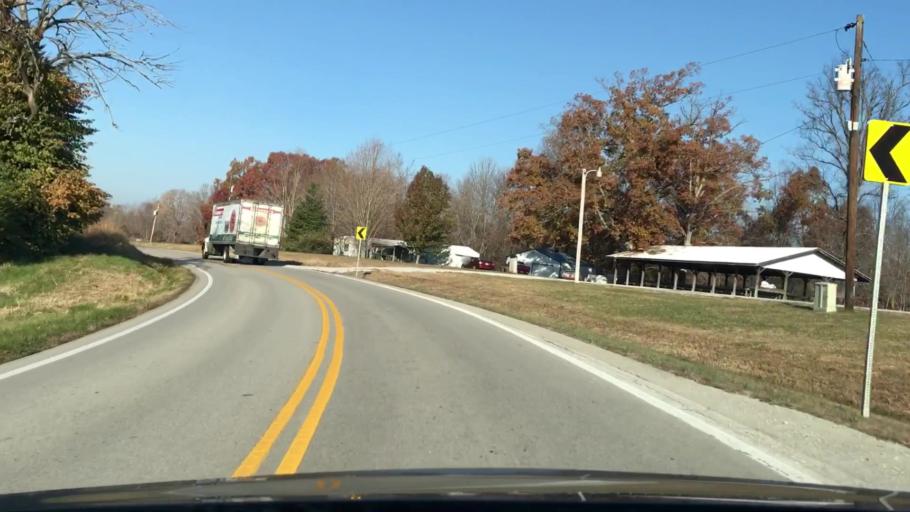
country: US
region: Kentucky
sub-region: Grayson County
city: Leitchfield
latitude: 37.3711
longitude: -86.2454
